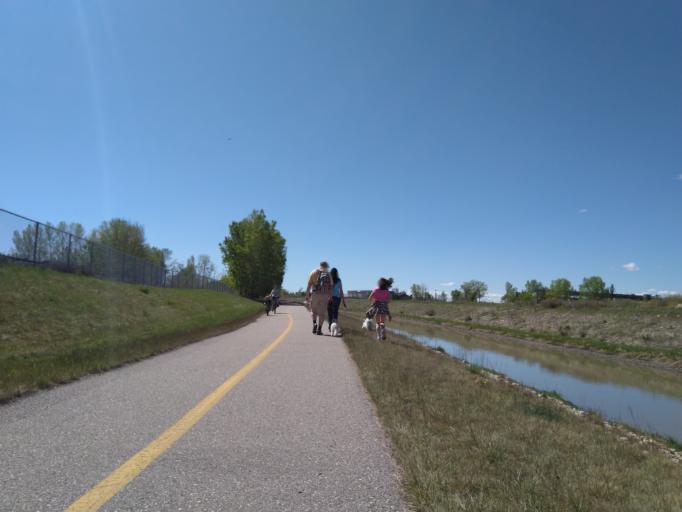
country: CA
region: Alberta
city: Calgary
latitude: 50.9770
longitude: -113.9926
